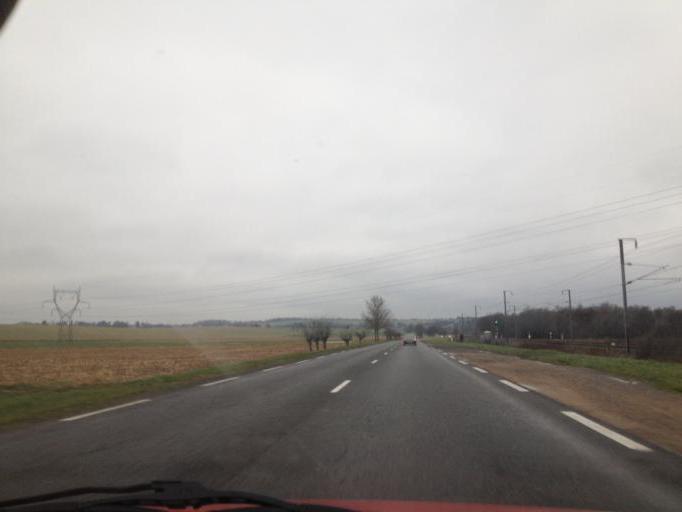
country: FR
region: Auvergne
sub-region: Departement de l'Allier
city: Varennes-sur-Allier
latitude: 46.2794
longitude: 3.4277
